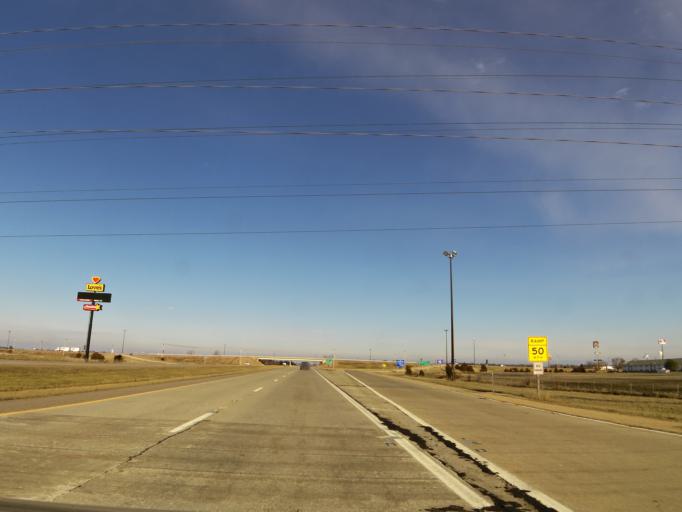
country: US
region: Illinois
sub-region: LaSalle County
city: Oglesby
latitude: 41.2911
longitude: -89.0824
